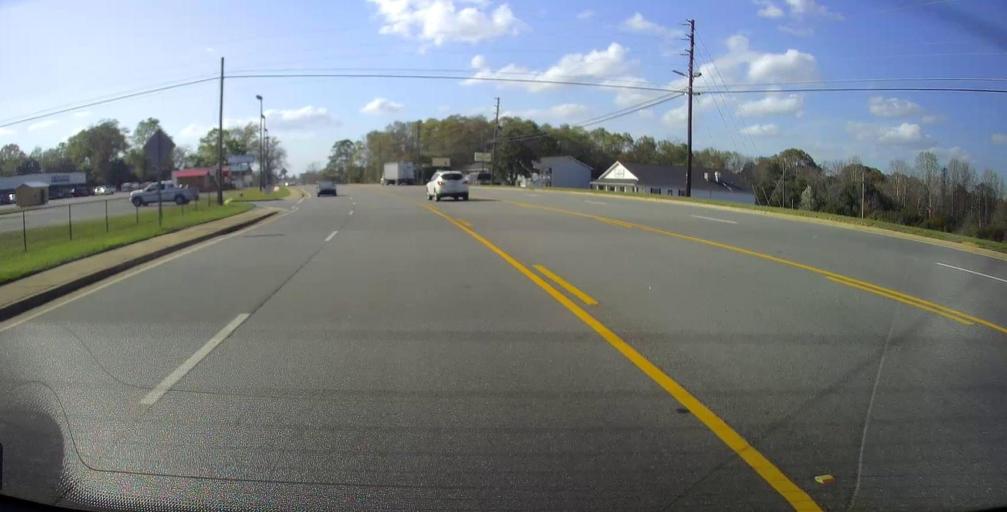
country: US
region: Georgia
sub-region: Telfair County
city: McRae
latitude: 32.0633
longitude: -82.8845
